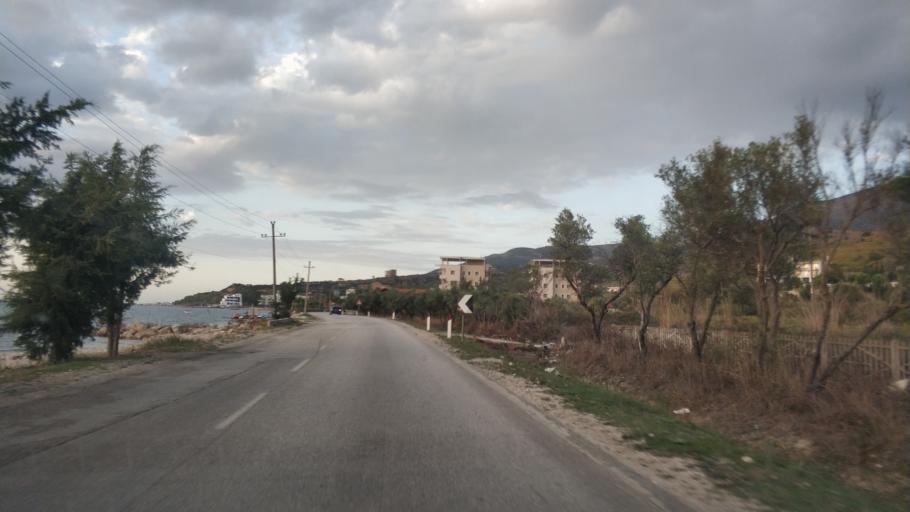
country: AL
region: Vlore
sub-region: Rrethi i Vlores
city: Orikum
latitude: 40.3480
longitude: 19.4856
